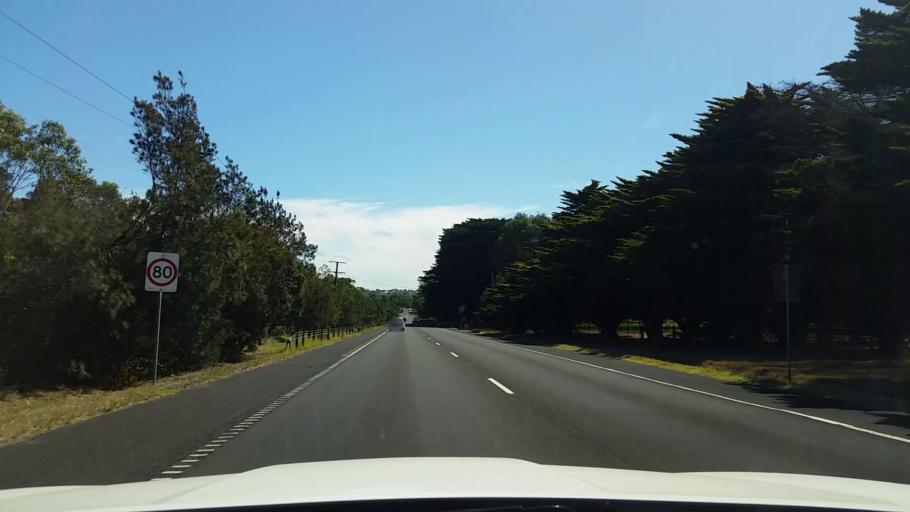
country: AU
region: Victoria
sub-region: Mornington Peninsula
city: Somerville
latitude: -38.2102
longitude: 145.1662
